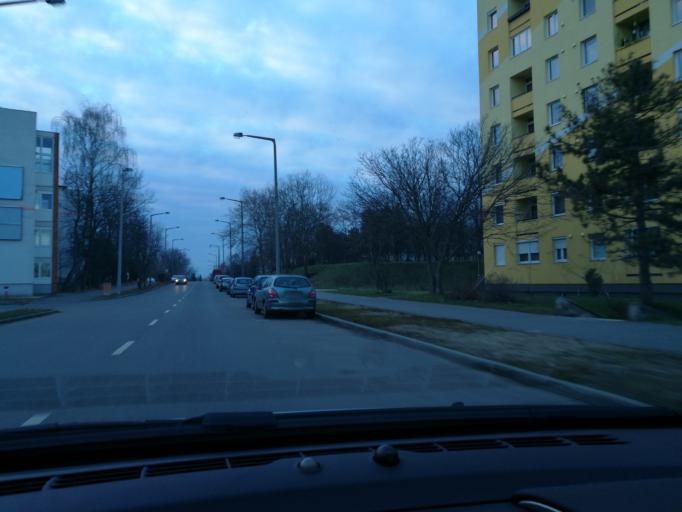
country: HU
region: Szabolcs-Szatmar-Bereg
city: Nyiregyhaza
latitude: 47.9697
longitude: 21.7232
